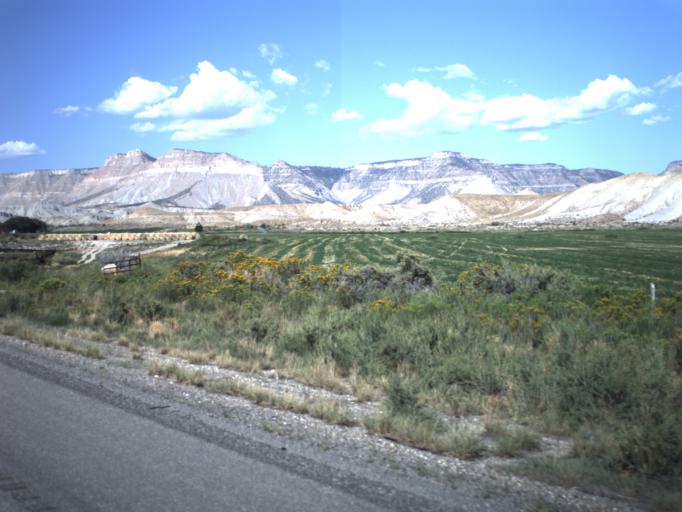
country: US
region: Utah
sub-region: Emery County
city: Orangeville
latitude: 39.1553
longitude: -111.0806
